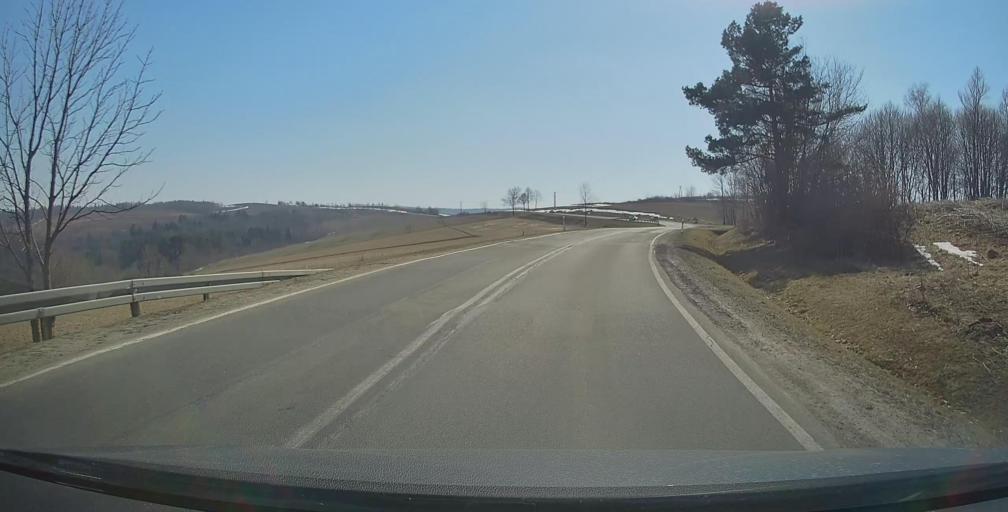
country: PL
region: Subcarpathian Voivodeship
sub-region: Powiat przemyski
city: Bircza
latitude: 49.6425
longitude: 22.4239
